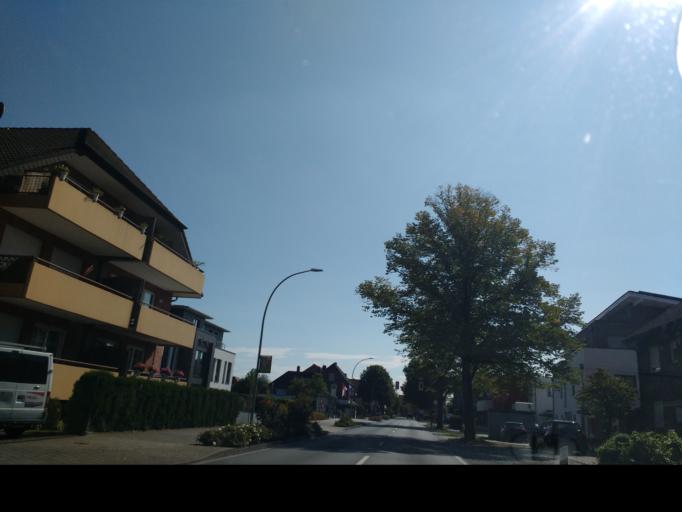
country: DE
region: North Rhine-Westphalia
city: Rietberg
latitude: 51.8133
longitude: 8.4234
